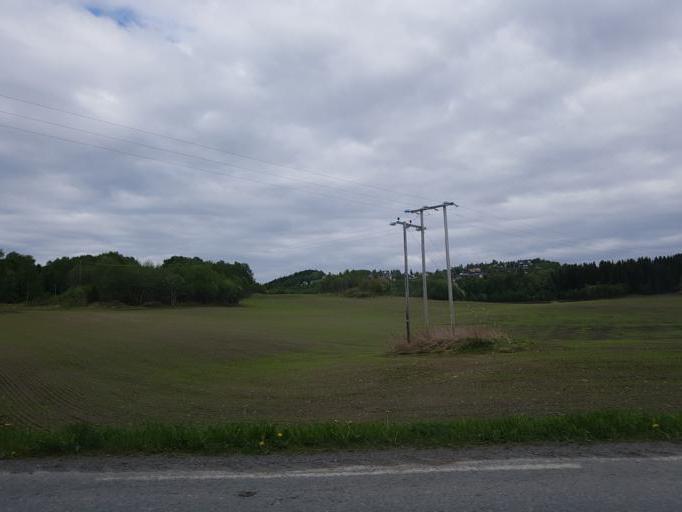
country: NO
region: Nord-Trondelag
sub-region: Levanger
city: Levanger
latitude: 63.7219
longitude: 11.2578
